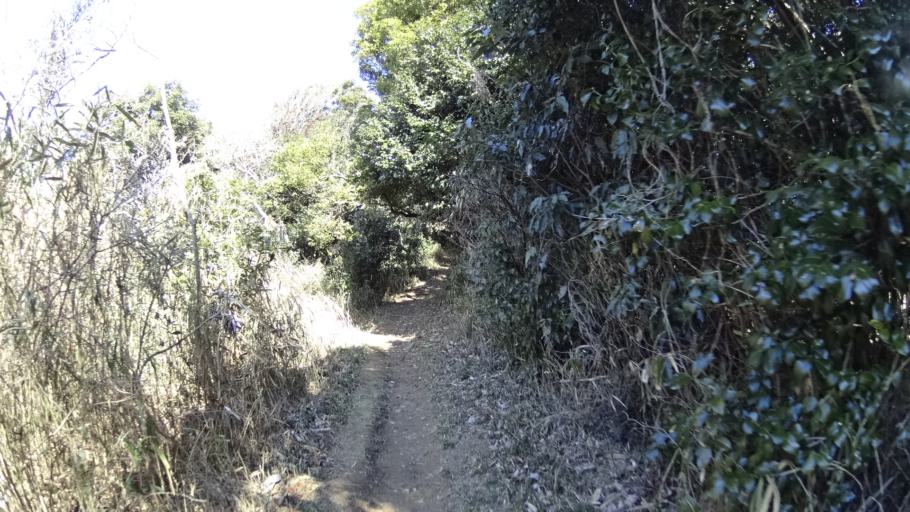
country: JP
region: Shizuoka
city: Kosai-shi
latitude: 34.7535
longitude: 137.4750
